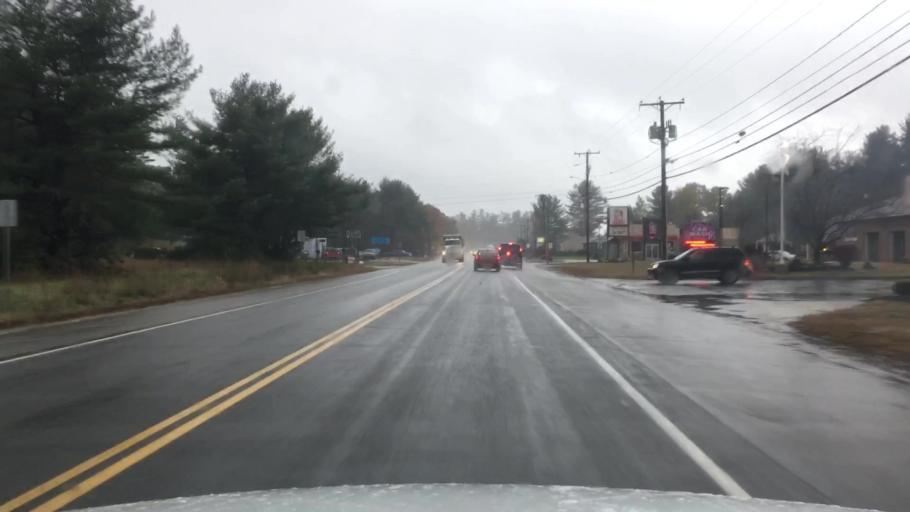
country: US
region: New Hampshire
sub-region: Strafford County
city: Rochester
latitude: 43.2585
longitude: -70.9791
